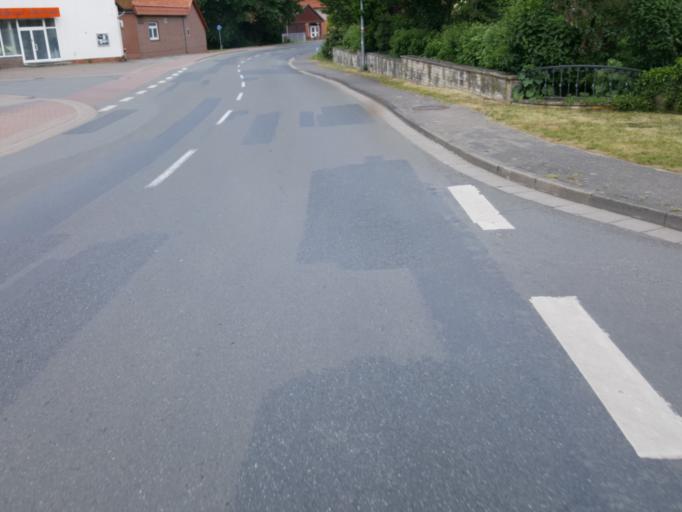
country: DE
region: Lower Saxony
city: Husum
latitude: 52.5901
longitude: 9.2489
